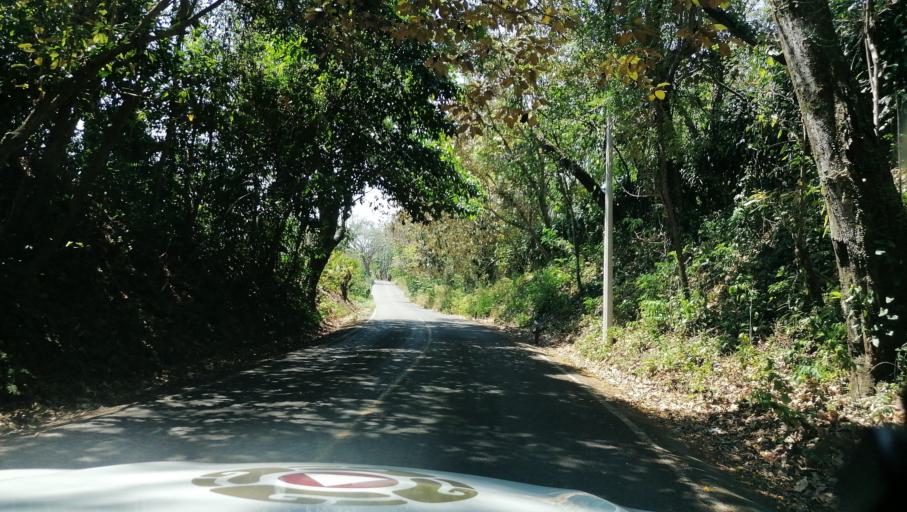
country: MX
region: Chiapas
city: Veinte de Noviembre
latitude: 15.0024
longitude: -92.2309
